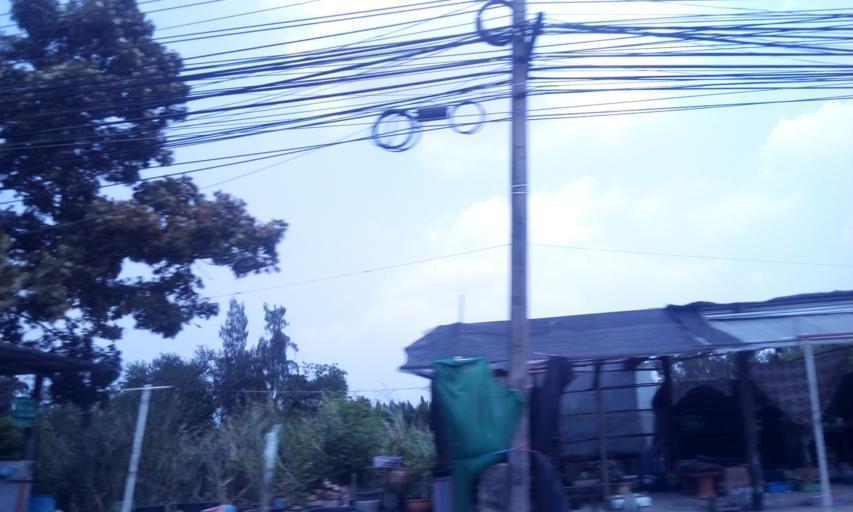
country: TH
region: Chachoengsao
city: Chachoengsao
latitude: 13.6754
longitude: 101.0839
